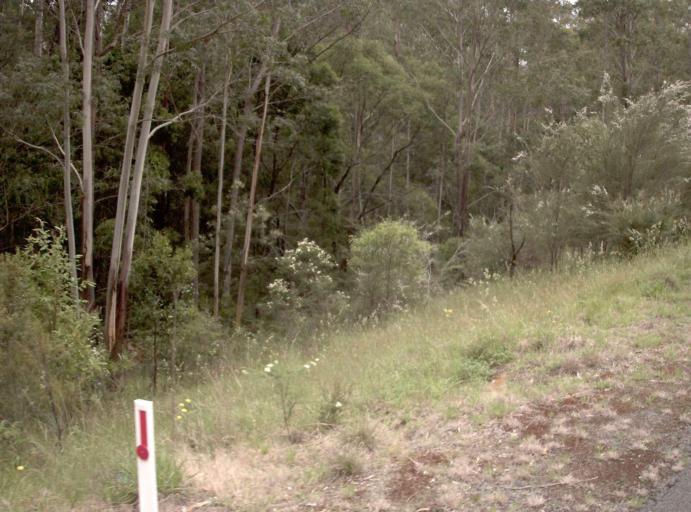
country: AU
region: New South Wales
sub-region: Bombala
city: Bombala
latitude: -37.2654
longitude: 149.2327
